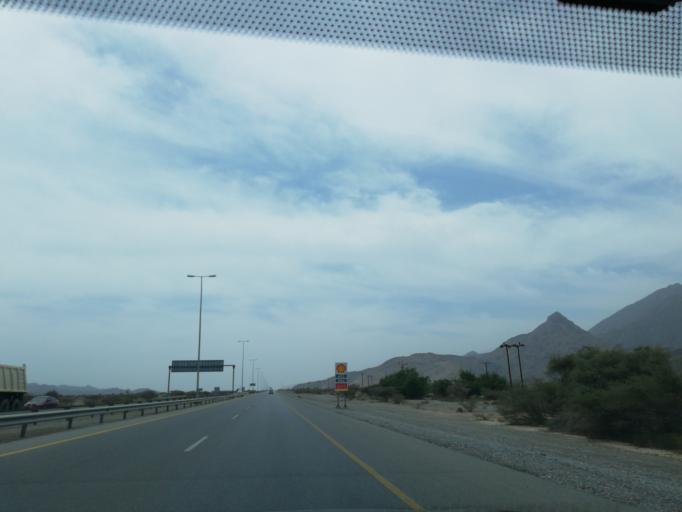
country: OM
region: Muhafazat ad Dakhiliyah
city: Izki
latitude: 23.0868
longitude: 57.8219
